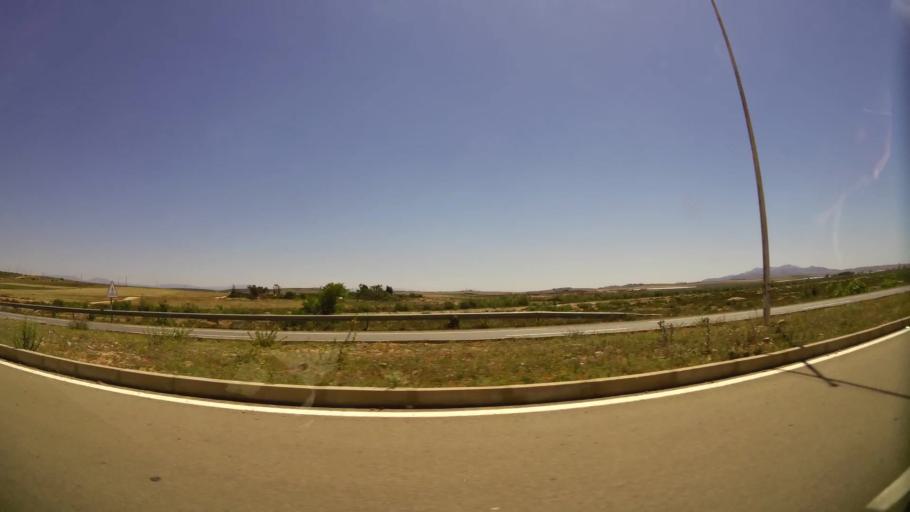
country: MA
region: Oriental
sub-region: Berkane-Taourirt
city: Madagh
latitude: 35.1006
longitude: -2.3343
